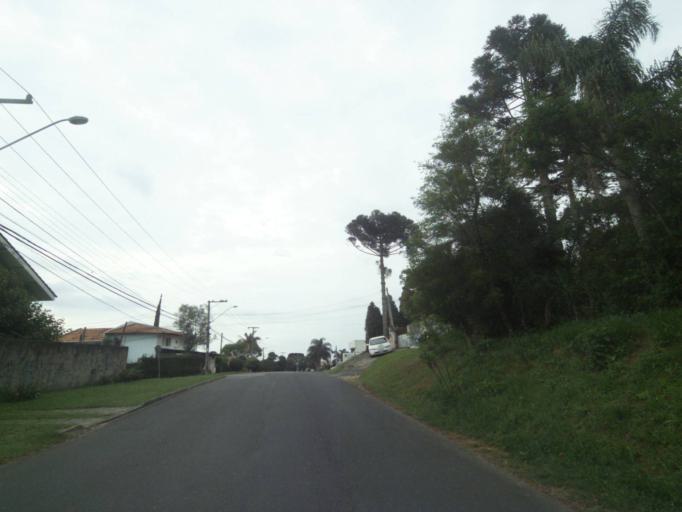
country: BR
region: Parana
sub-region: Curitiba
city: Curitiba
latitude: -25.3954
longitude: -49.2948
